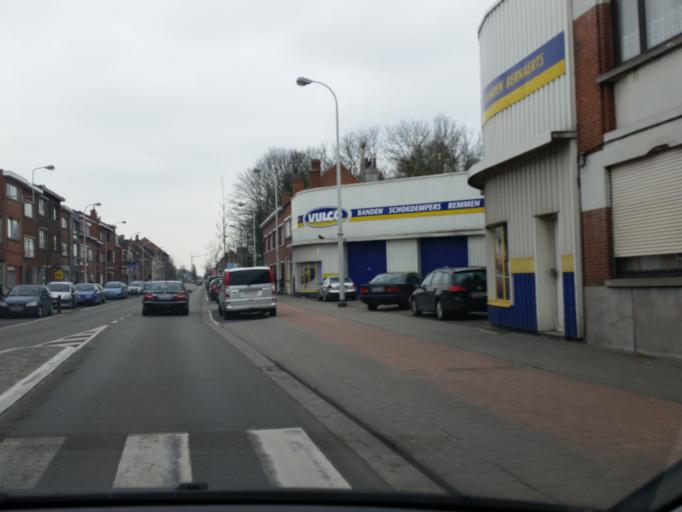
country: BE
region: Flanders
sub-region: Provincie Antwerpen
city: Mechelen
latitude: 51.0149
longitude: 4.5001
